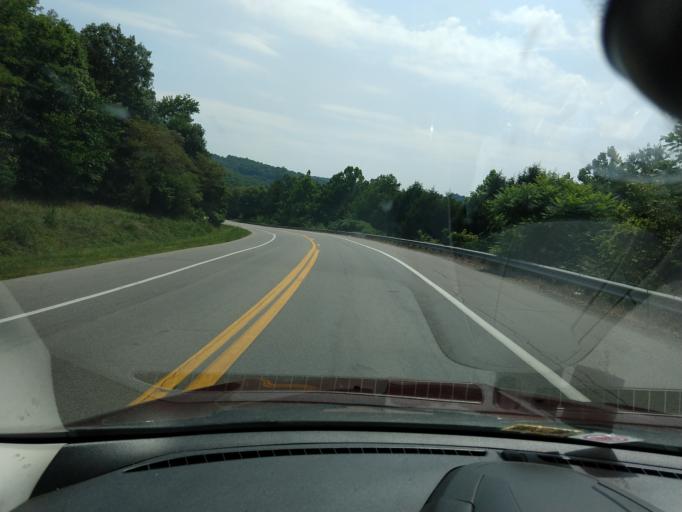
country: US
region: West Virginia
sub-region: Jackson County
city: Ravenswood
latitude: 38.8593
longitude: -81.8166
